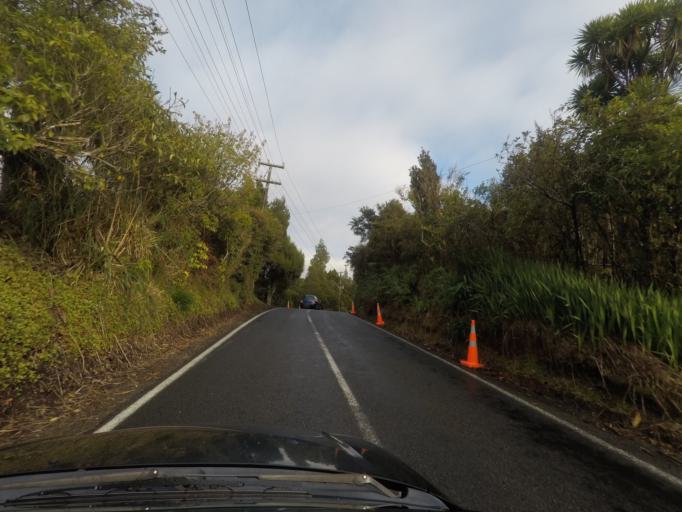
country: NZ
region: Auckland
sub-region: Auckland
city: Waitakere
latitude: -36.9171
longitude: 174.5950
